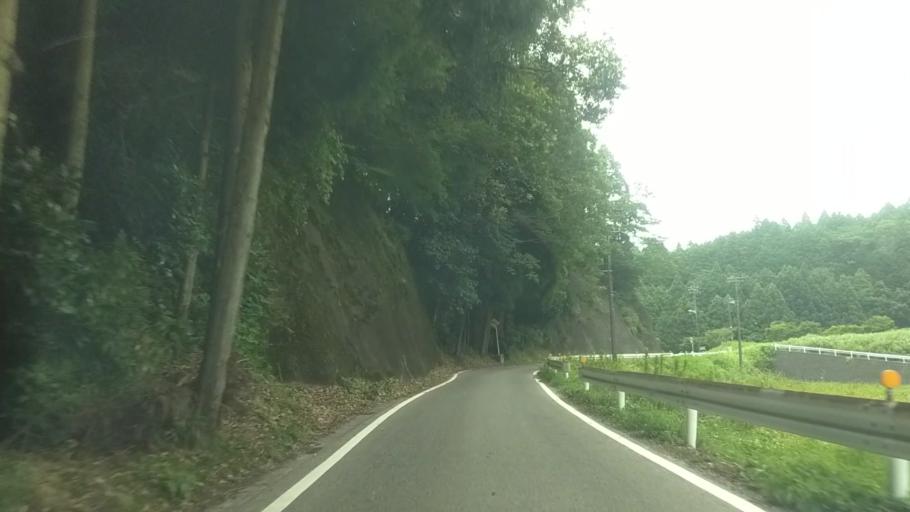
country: JP
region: Chiba
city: Kawaguchi
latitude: 35.2262
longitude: 140.1498
